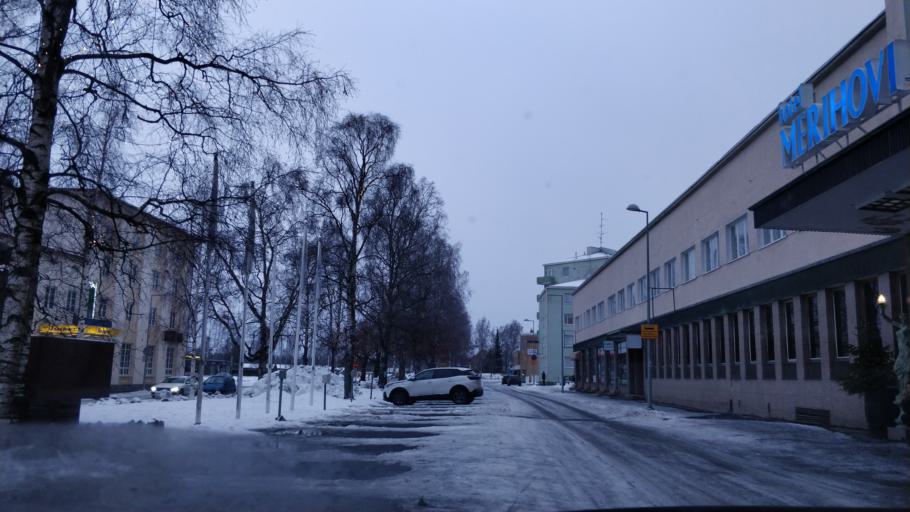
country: FI
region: Lapland
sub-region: Kemi-Tornio
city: Kemi
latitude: 65.7373
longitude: 24.5626
